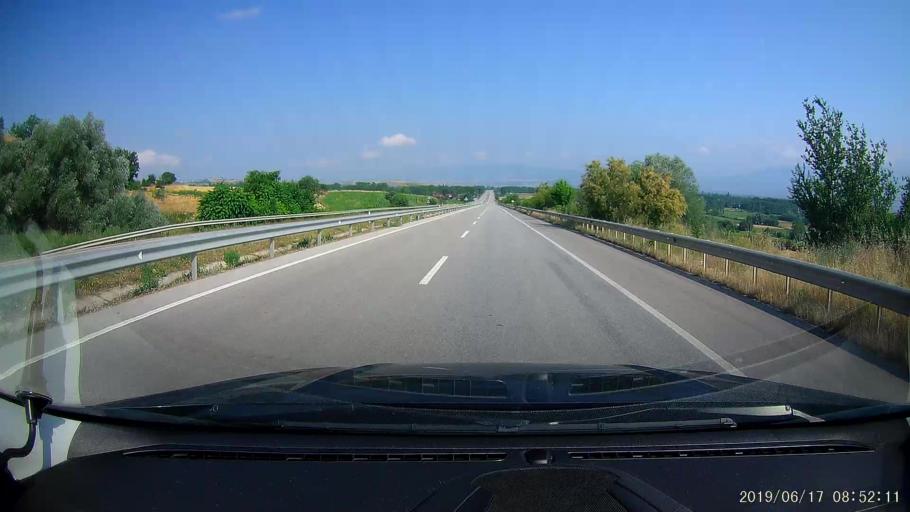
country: TR
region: Tokat
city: Erbaa
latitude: 40.6941
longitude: 36.5008
